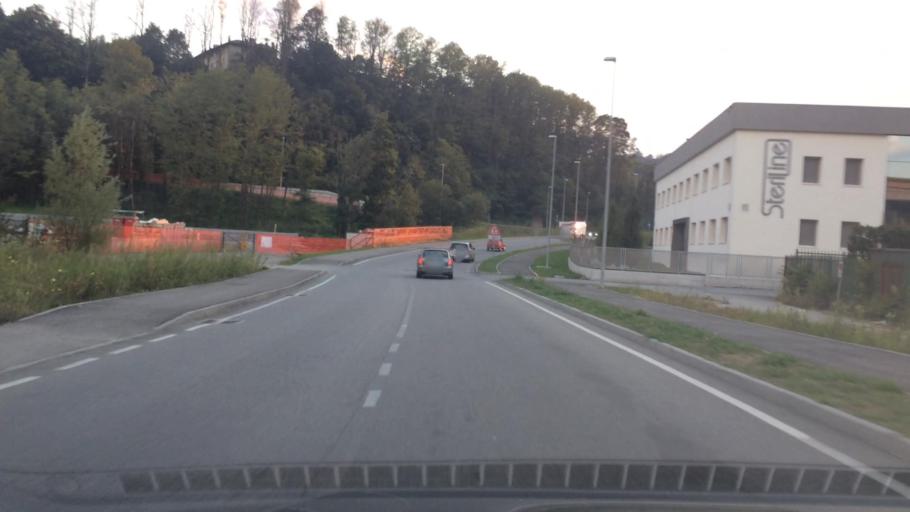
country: IT
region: Lombardy
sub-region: Provincia di Como
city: Como
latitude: 45.7790
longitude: 9.0769
